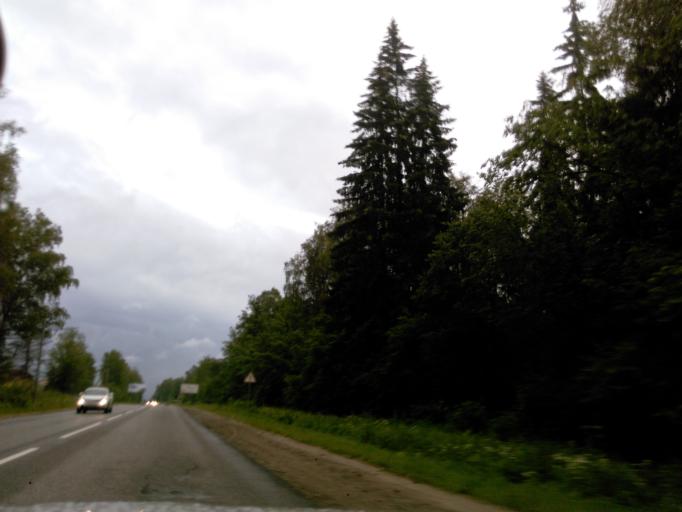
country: RU
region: Moskovskaya
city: Povarovo
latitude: 56.0312
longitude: 36.9762
